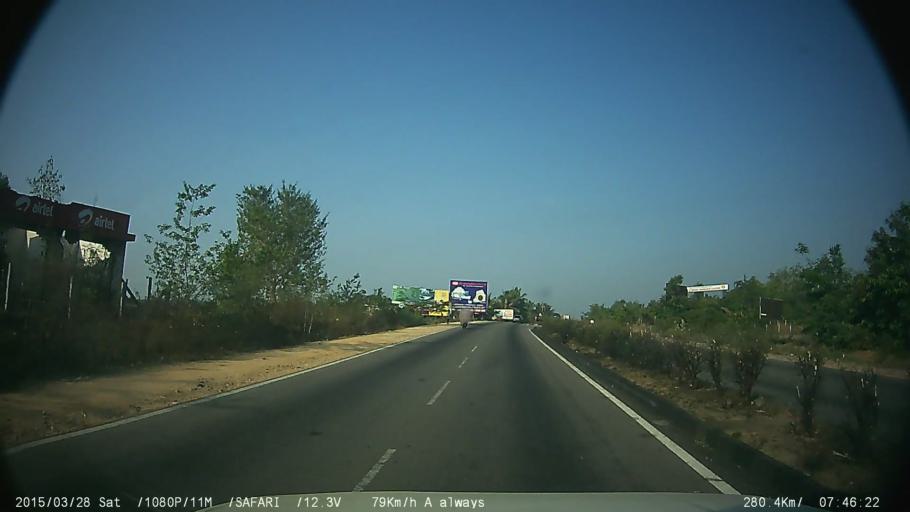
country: IN
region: Karnataka
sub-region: Mandya
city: Mandya
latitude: 12.4919
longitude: 76.7872
